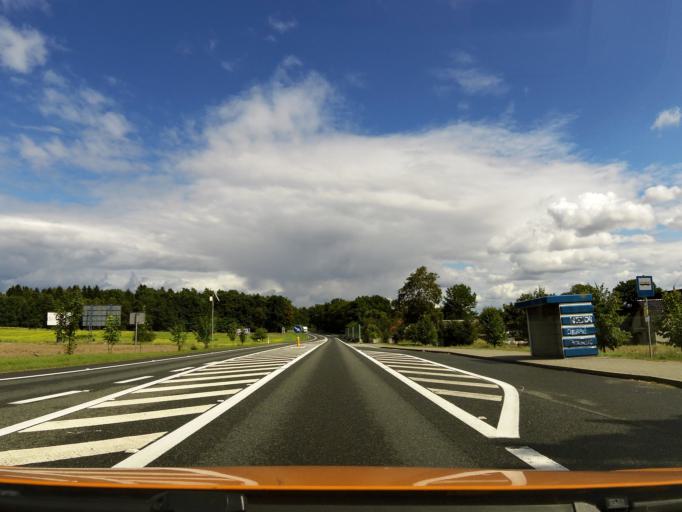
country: PL
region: West Pomeranian Voivodeship
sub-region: Powiat goleniowski
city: Osina
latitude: 53.6330
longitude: 15.0161
